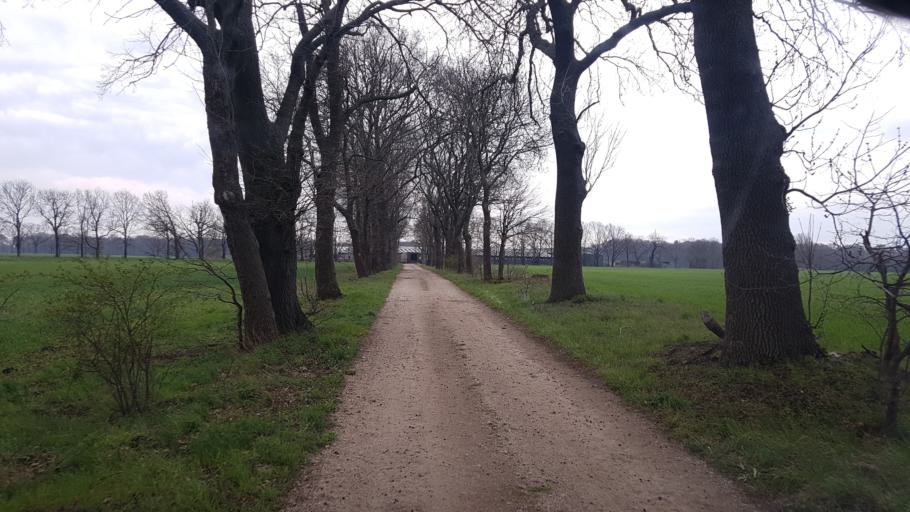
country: DE
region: Brandenburg
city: Bronkow
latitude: 51.6171
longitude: 13.9063
